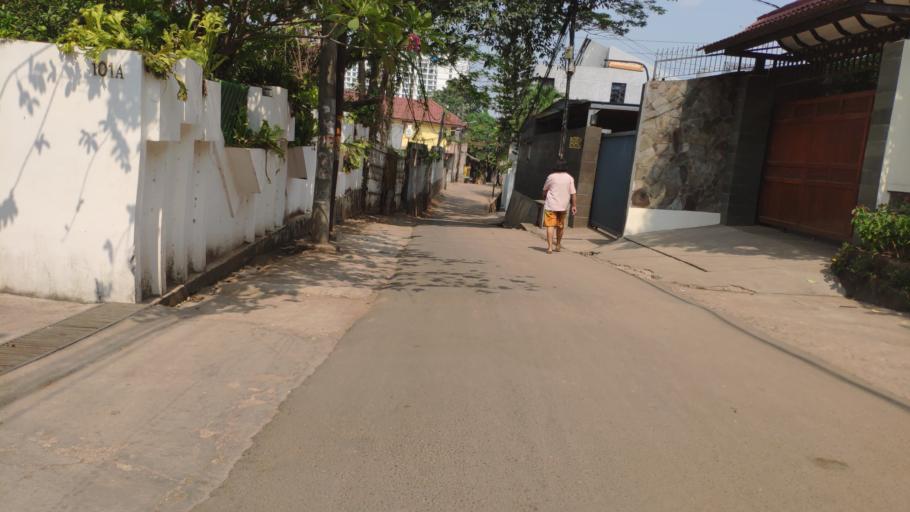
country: ID
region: Jakarta Raya
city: Jakarta
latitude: -6.2544
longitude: 106.8225
